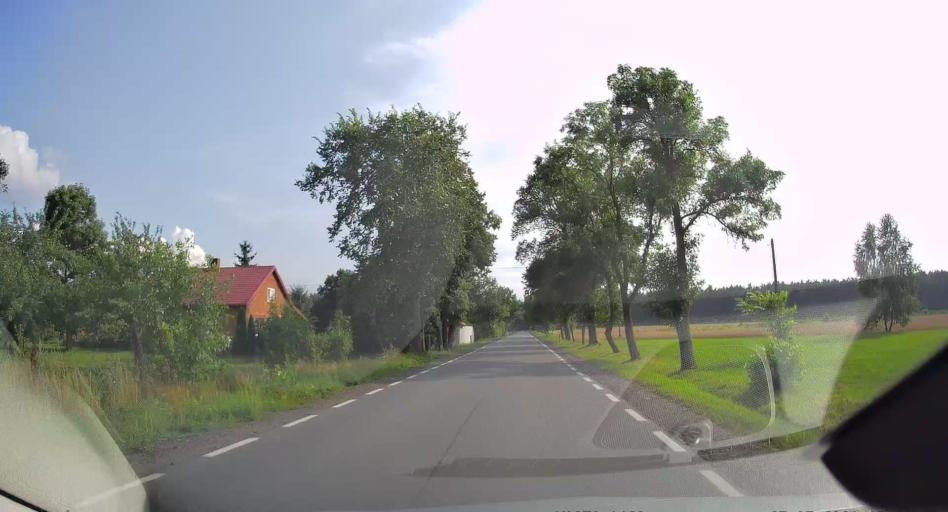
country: PL
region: Lodz Voivodeship
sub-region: Powiat tomaszowski
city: Rzeczyca
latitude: 51.5808
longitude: 20.2844
